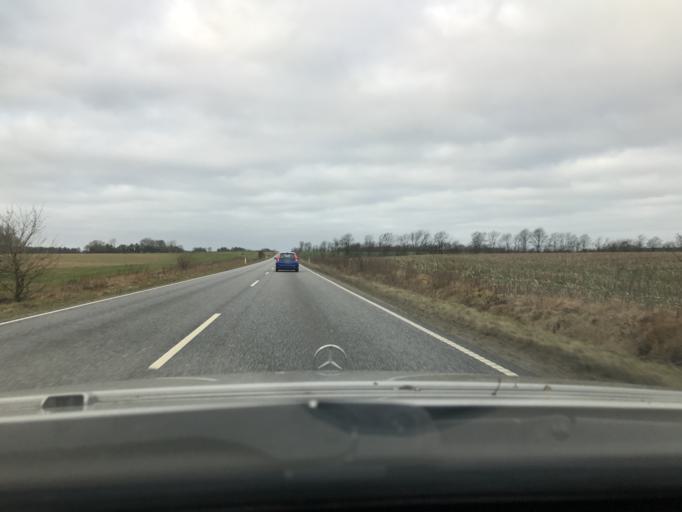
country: DK
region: South Denmark
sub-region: Tonder Kommune
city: Toftlund
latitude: 55.1108
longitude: 9.1749
